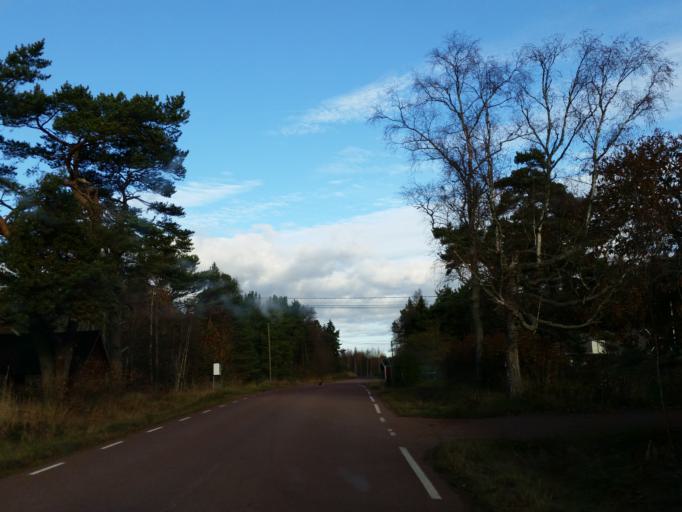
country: AX
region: Alands skaergard
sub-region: Foegloe
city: Foegloe
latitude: 60.0392
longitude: 20.5355
